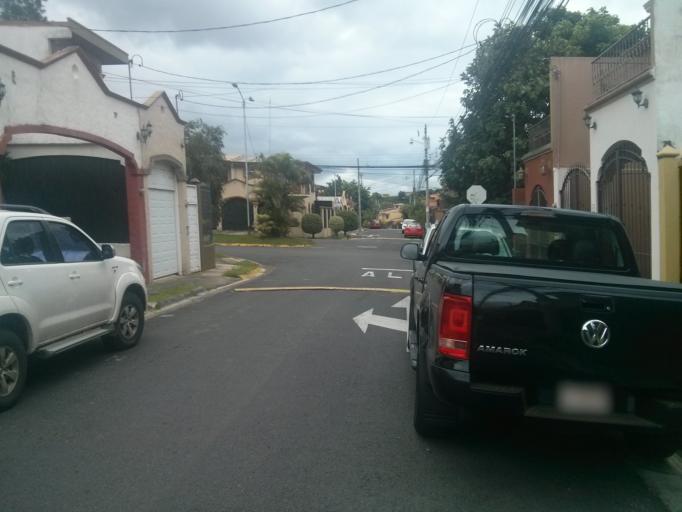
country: CR
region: San Jose
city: Curridabat
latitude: 9.9009
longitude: -84.0524
